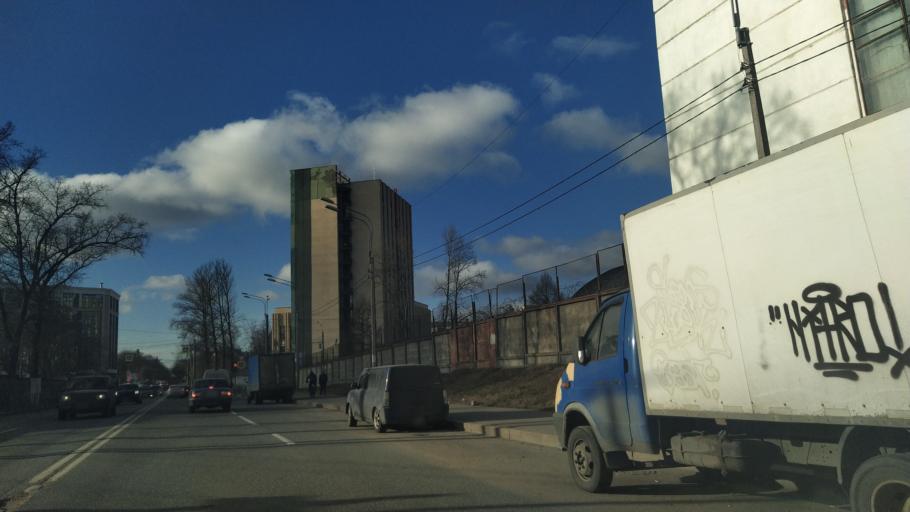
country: RU
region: St.-Petersburg
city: Kushelevka
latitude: 59.9937
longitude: 30.3618
